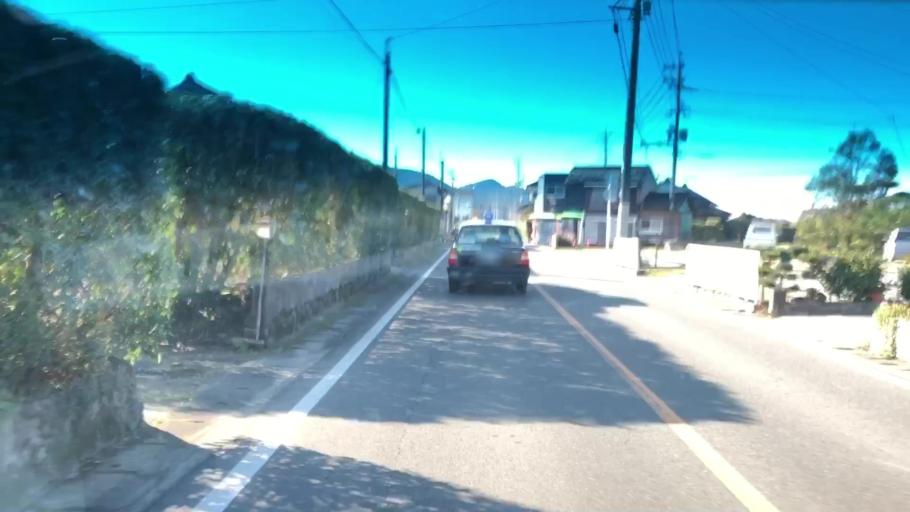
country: JP
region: Kagoshima
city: Satsumasendai
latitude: 31.8241
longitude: 130.2532
